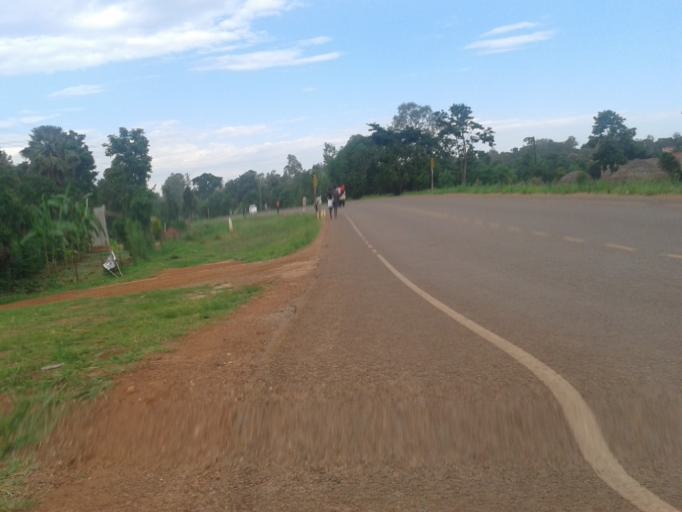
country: UG
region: Northern Region
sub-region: Gulu District
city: Gulu
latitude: 2.7631
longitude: 32.2725
